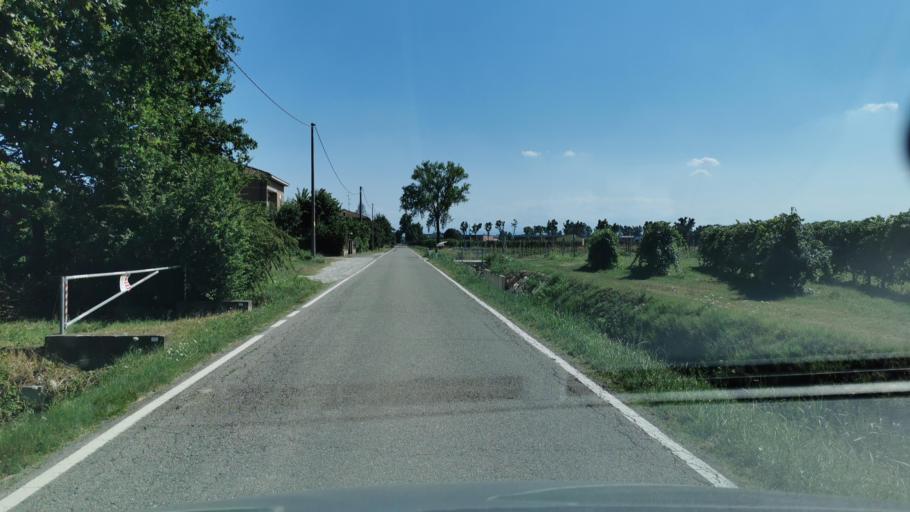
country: IT
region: Emilia-Romagna
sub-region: Provincia di Modena
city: Limidi
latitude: 44.7711
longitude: 10.9172
